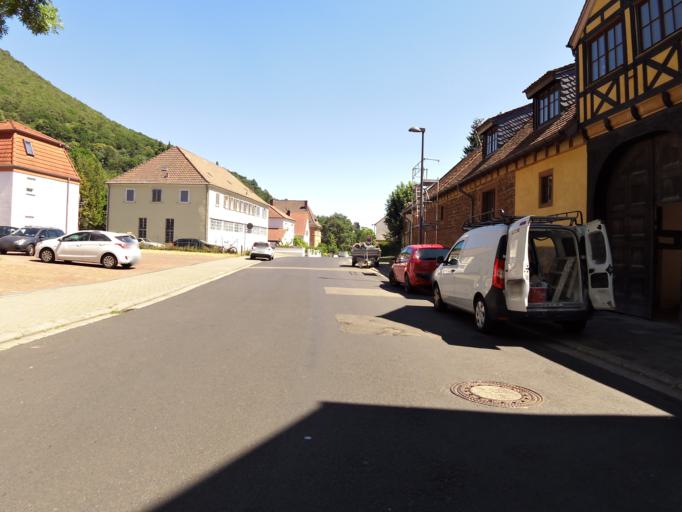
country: DE
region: Rheinland-Pfalz
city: Neustadt
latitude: 49.3571
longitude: 8.1128
